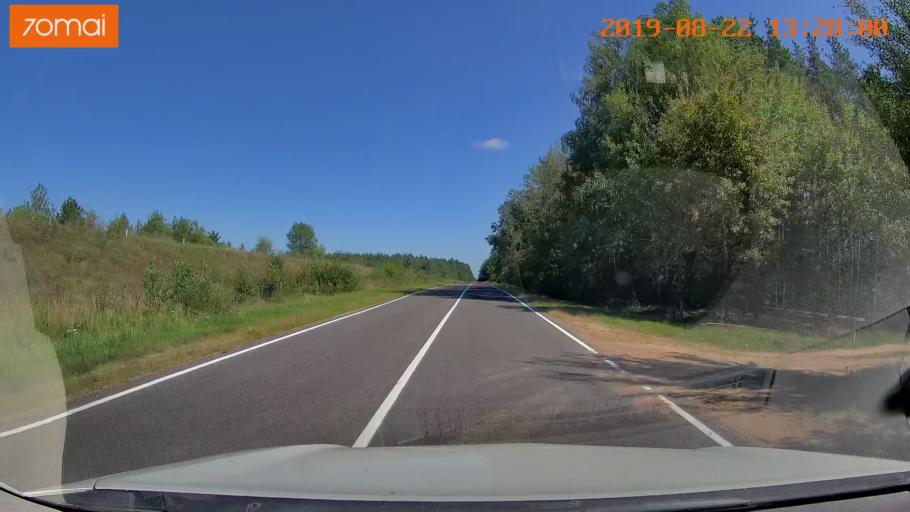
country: BY
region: Minsk
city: Staryya Darohi
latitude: 53.2106
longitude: 28.0977
